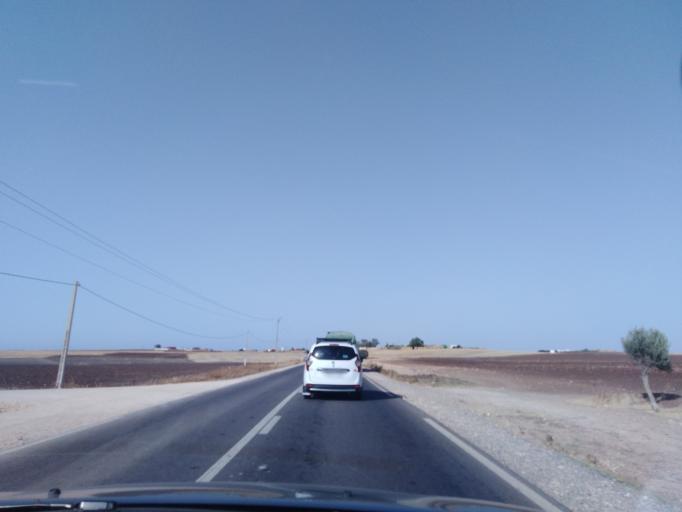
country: MA
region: Doukkala-Abda
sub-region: Safi
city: Safi
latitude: 32.2738
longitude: -8.9344
